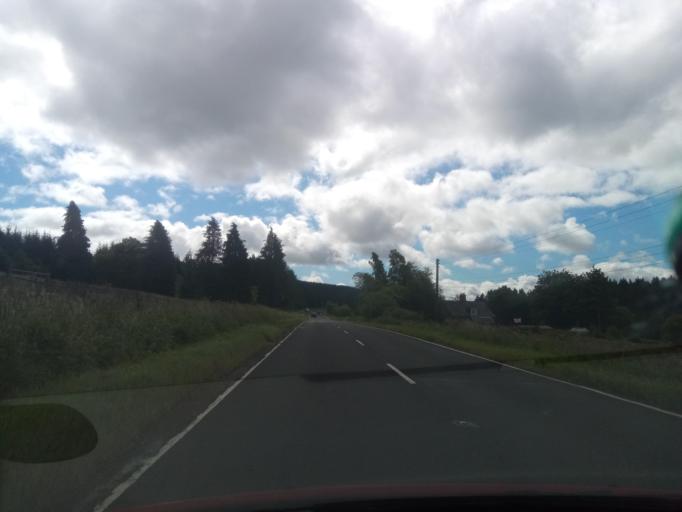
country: GB
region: England
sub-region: Northumberland
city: Rochester
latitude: 55.3113
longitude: -2.3560
